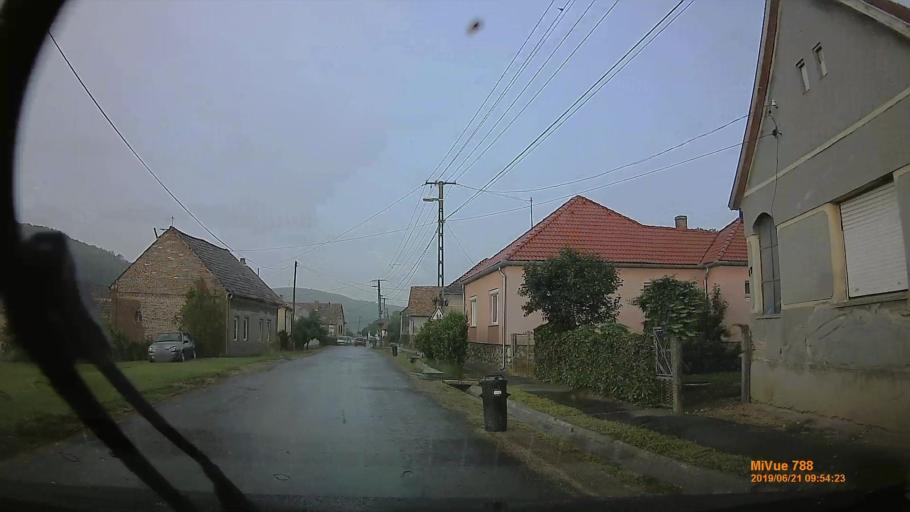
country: HU
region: Baranya
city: Sasd
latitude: 46.2316
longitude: 17.9970
